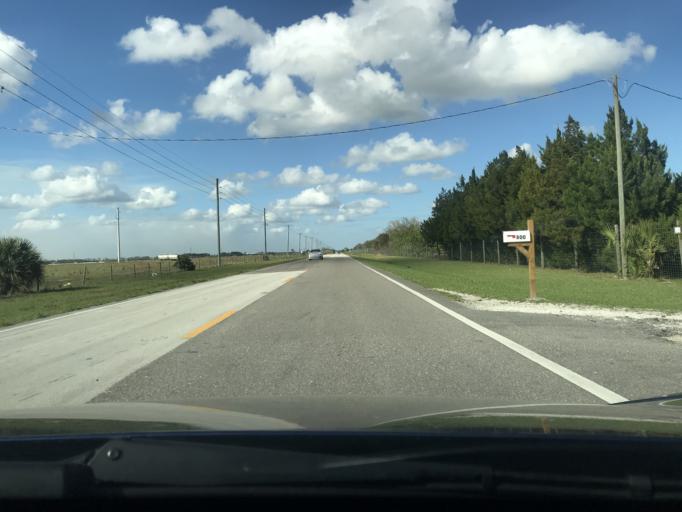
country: US
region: Florida
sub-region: Okeechobee County
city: Taylor Creek
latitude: 27.2387
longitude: -80.6944
